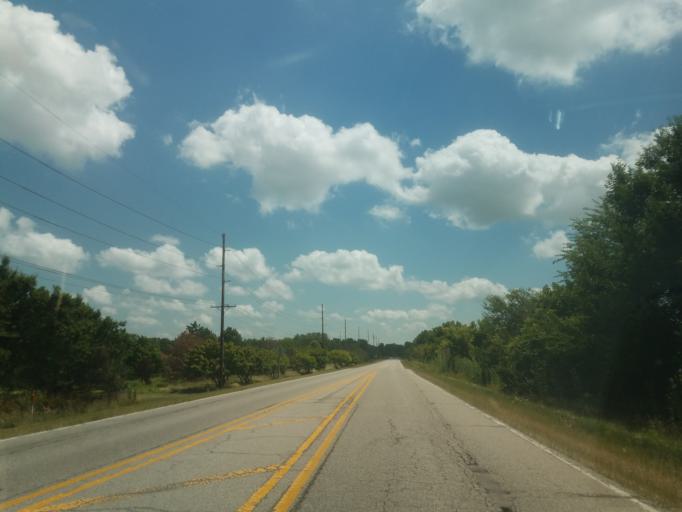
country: US
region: Illinois
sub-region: McLean County
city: Bloomington
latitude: 40.4936
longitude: -89.0193
